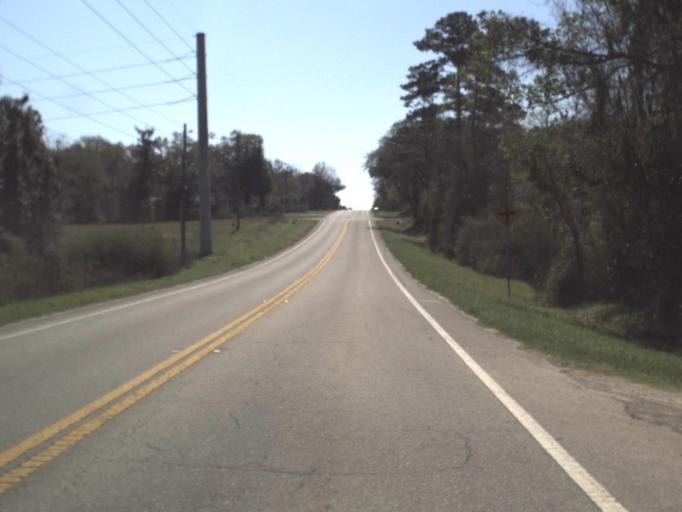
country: US
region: Florida
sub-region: Jefferson County
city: Monticello
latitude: 30.4020
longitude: -84.0193
